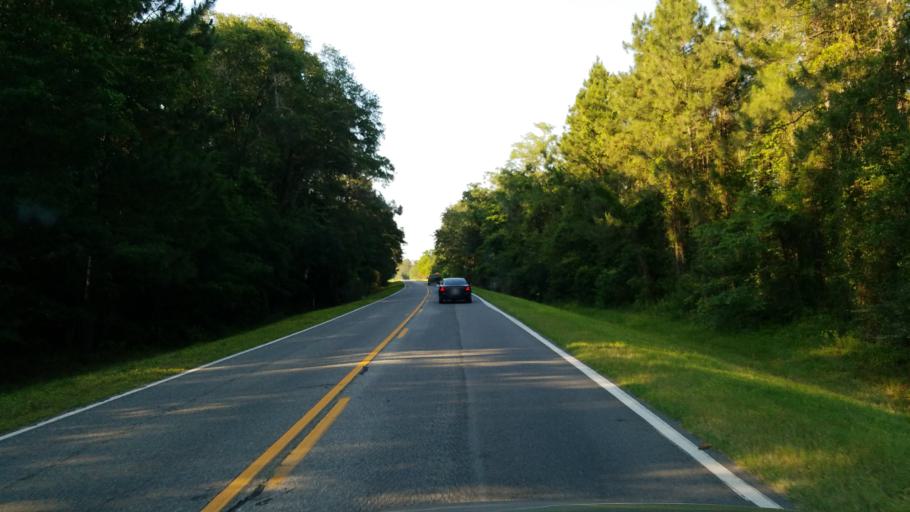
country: US
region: Georgia
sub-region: Lanier County
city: Lakeland
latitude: 30.9840
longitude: -83.0731
